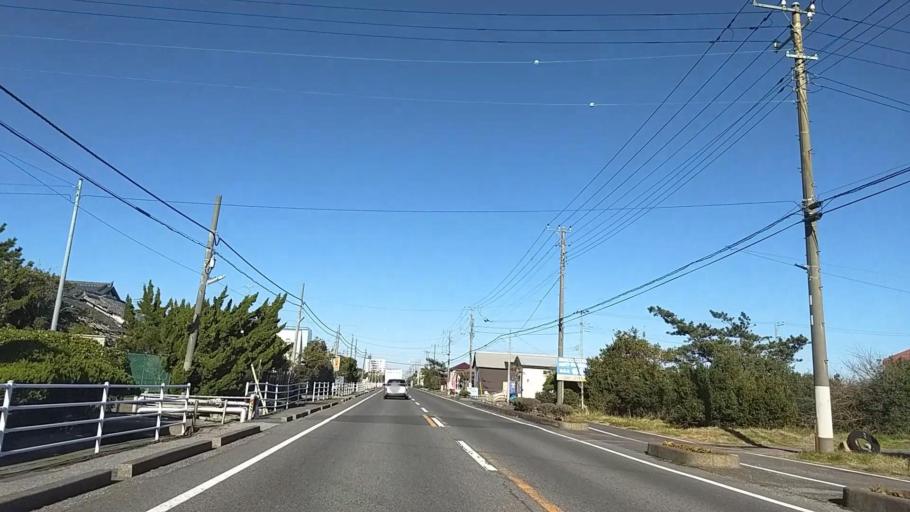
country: JP
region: Chiba
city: Togane
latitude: 35.4799
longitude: 140.4171
